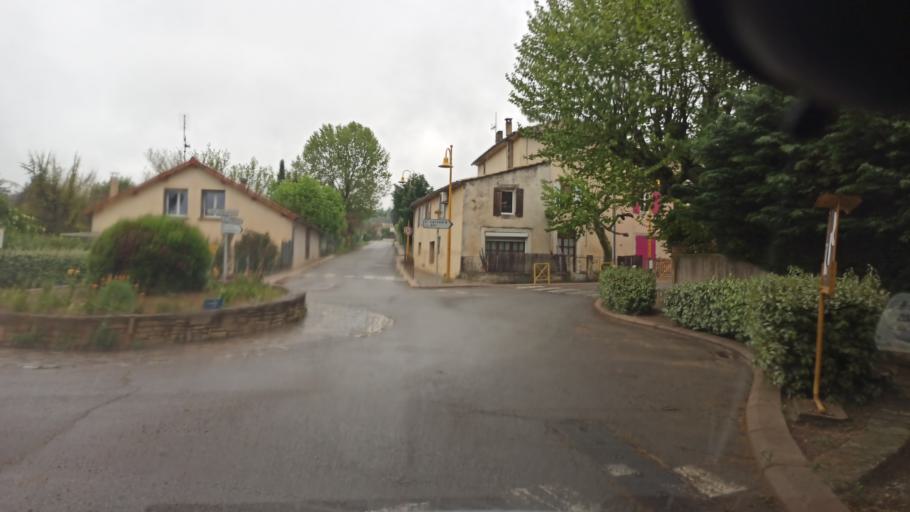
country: FR
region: Provence-Alpes-Cote d'Azur
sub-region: Departement du Vaucluse
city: Gargas
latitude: 43.9039
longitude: 5.3576
